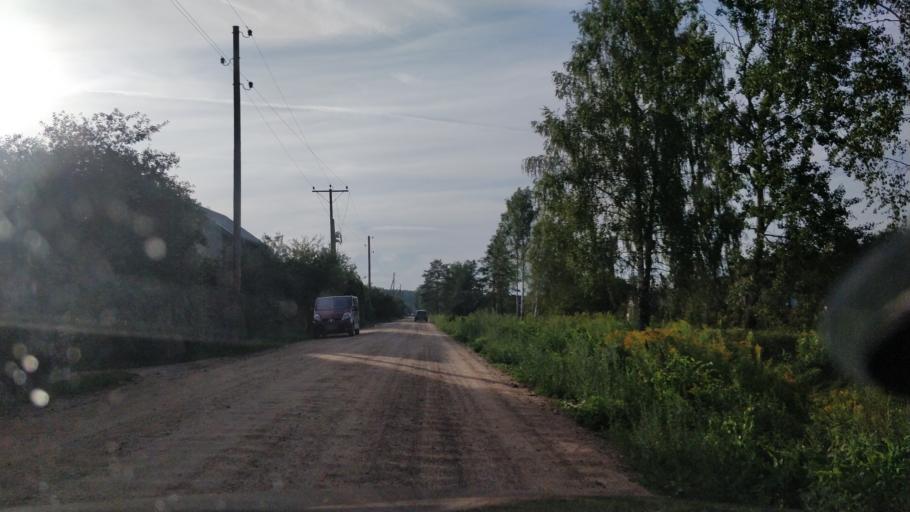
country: LV
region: Incukalns
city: Incukalns
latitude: 57.0981
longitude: 24.7547
